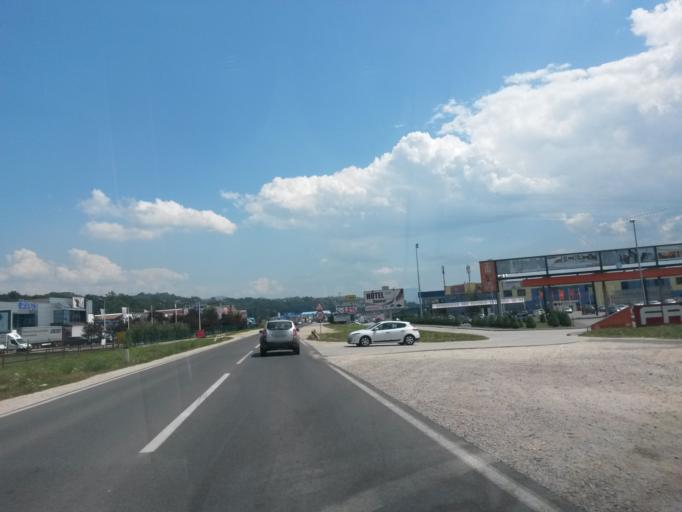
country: BA
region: Federation of Bosnia and Herzegovina
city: Vitez
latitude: 44.1701
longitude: 17.7786
